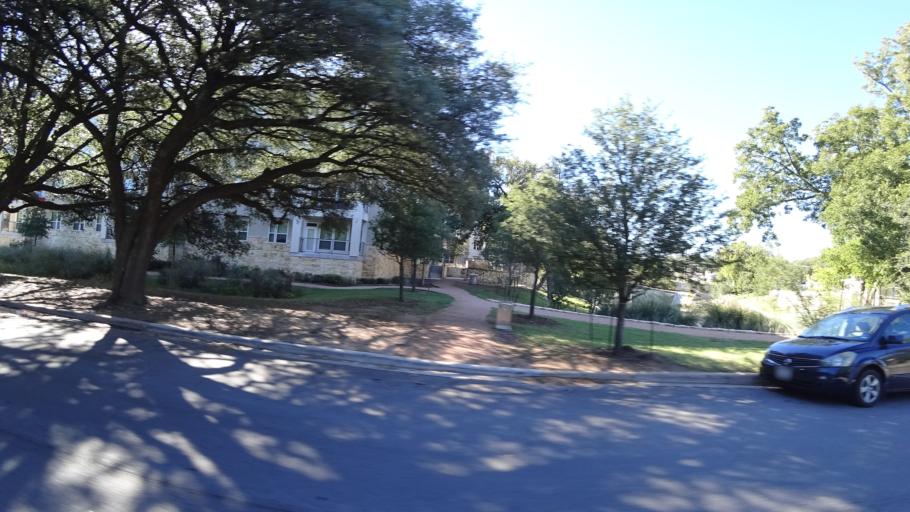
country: US
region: Texas
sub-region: Travis County
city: Austin
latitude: 30.2449
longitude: -97.7285
